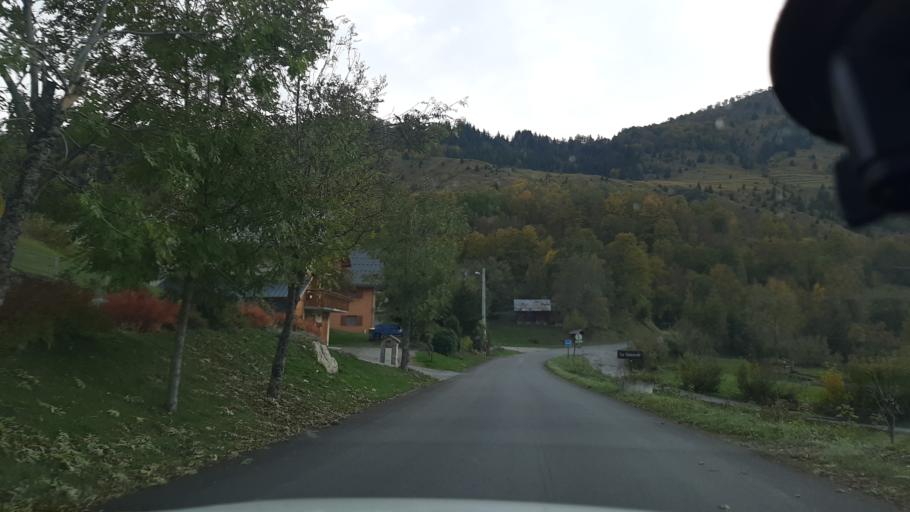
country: FR
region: Rhone-Alpes
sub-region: Departement de la Savoie
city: Villargondran
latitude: 45.1972
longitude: 6.3326
